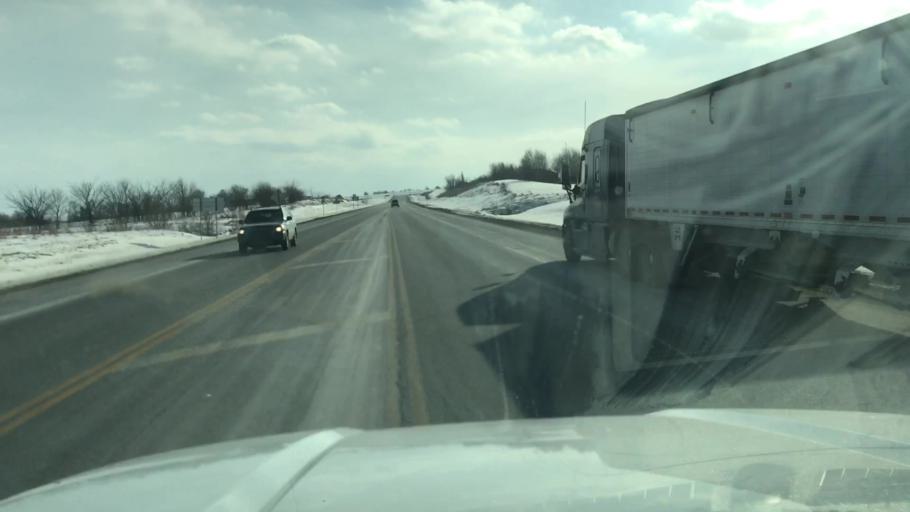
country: US
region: Missouri
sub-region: Nodaway County
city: Maryville
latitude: 40.3439
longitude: -94.8524
